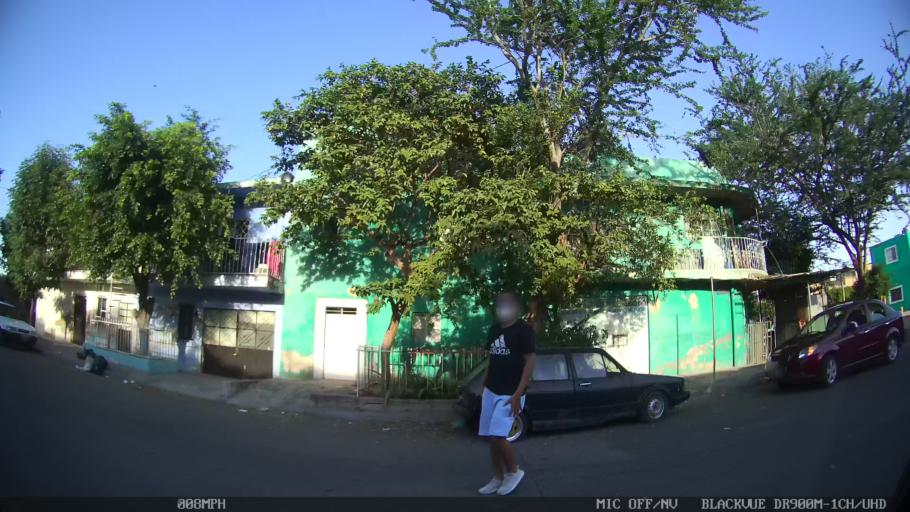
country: MX
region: Jalisco
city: Tlaquepaque
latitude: 20.7009
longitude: -103.3031
